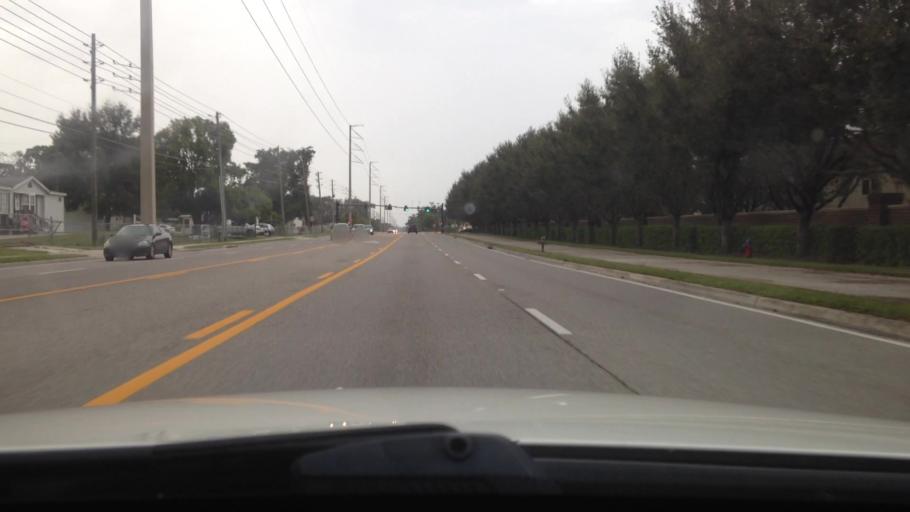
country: US
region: Florida
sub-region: Orange County
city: Apopka
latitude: 28.7116
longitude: -81.5091
